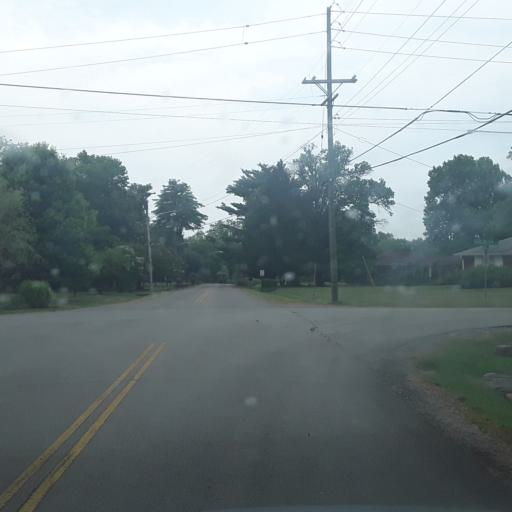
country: US
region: Tennessee
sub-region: Davidson County
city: Oak Hill
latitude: 36.0710
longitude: -86.7441
